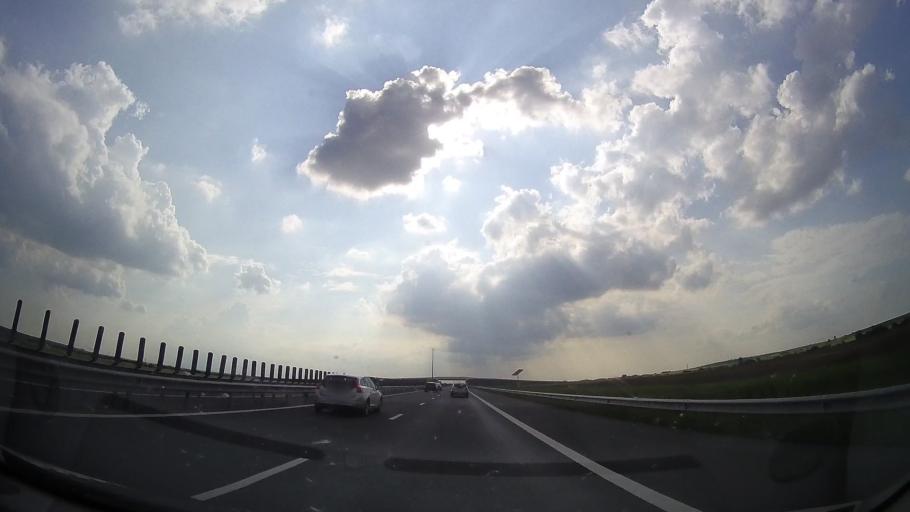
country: RO
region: Timis
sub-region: Oras Recas
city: Recas
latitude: 45.8136
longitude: 21.5017
